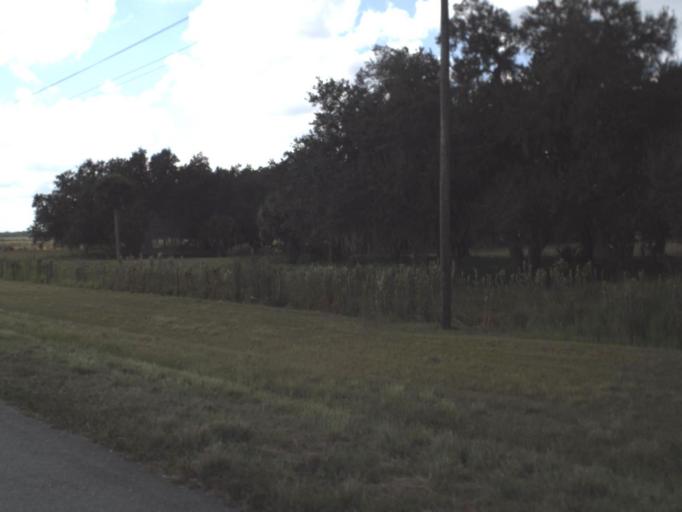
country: US
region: Florida
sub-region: Okeechobee County
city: Okeechobee
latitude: 27.3835
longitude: -81.0399
